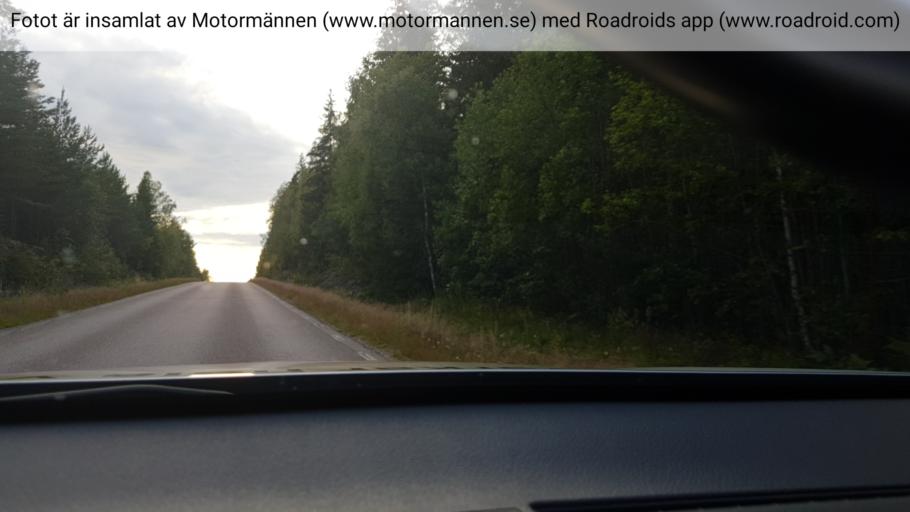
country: SE
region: Vaermland
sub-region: Forshaga Kommun
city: Deje
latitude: 59.7450
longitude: 13.3915
